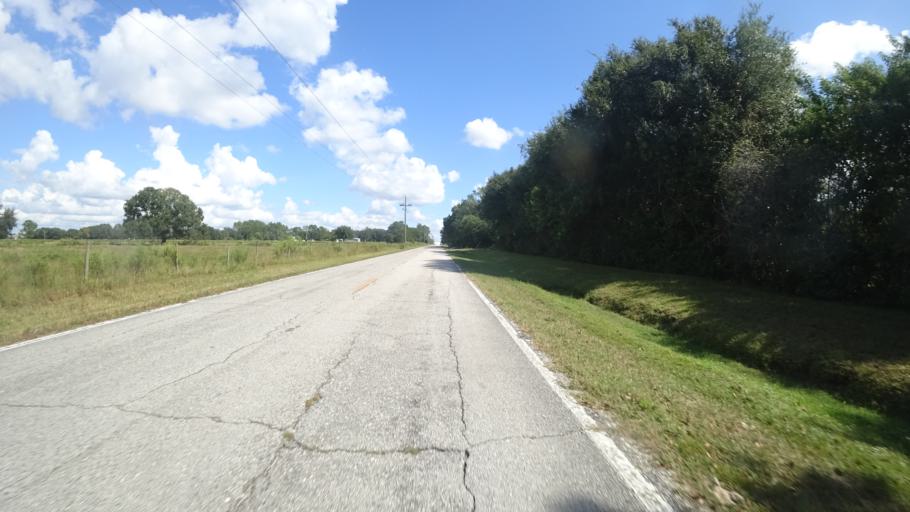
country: US
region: Florida
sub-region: Manatee County
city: Ellenton
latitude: 27.4878
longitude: -82.3732
